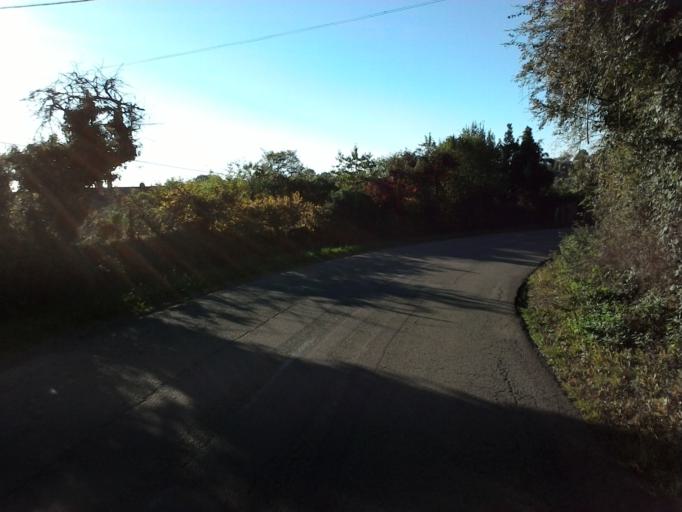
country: FR
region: Bourgogne
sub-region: Departement de la Cote-d'Or
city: Saulieu
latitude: 47.2746
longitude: 4.2355
